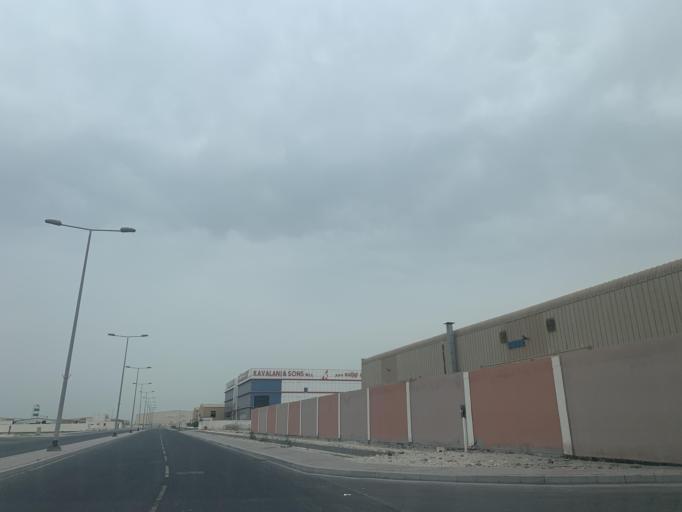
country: BH
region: Muharraq
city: Al Hadd
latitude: 26.2098
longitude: 50.6824
